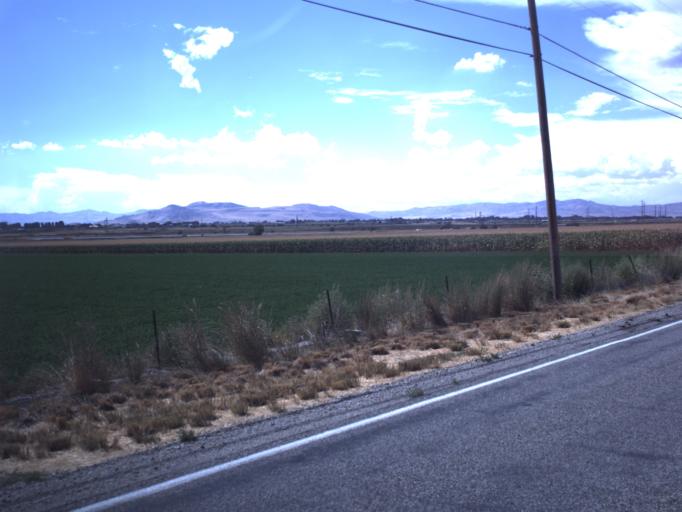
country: US
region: Utah
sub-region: Box Elder County
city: Honeyville
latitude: 41.6003
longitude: -112.0501
